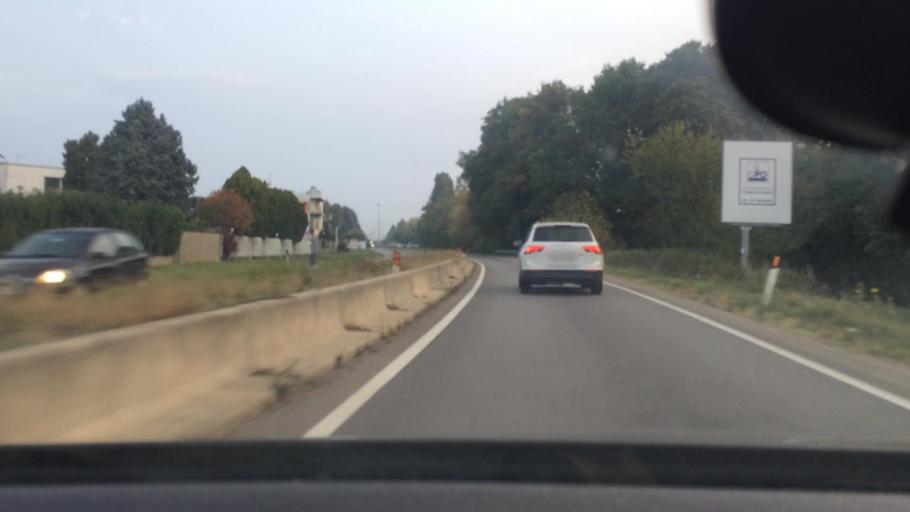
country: IT
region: Lombardy
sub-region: Citta metropolitana di Milano
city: Villa Cortese
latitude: 45.5625
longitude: 8.8950
